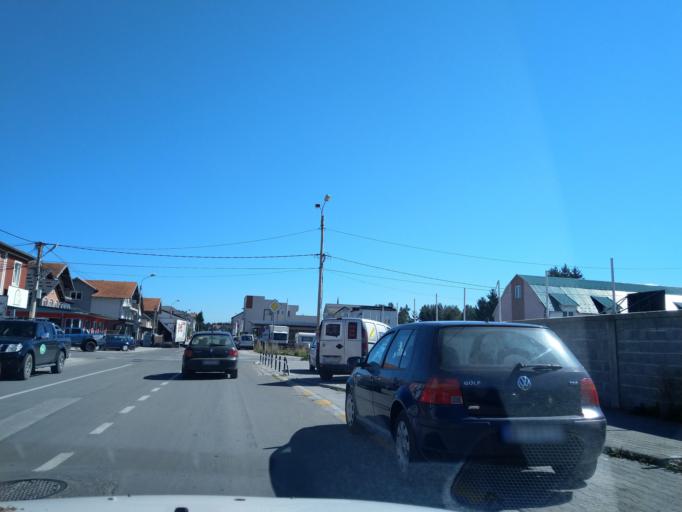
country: RS
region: Central Serbia
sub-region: Zlatiborski Okrug
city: Sjenica
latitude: 43.2741
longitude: 20.0061
